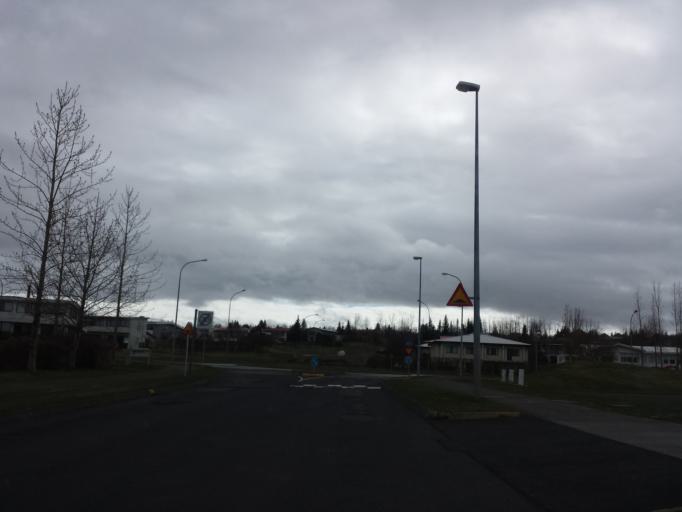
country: IS
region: Capital Region
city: Gardabaer
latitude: 64.0930
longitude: -21.9045
